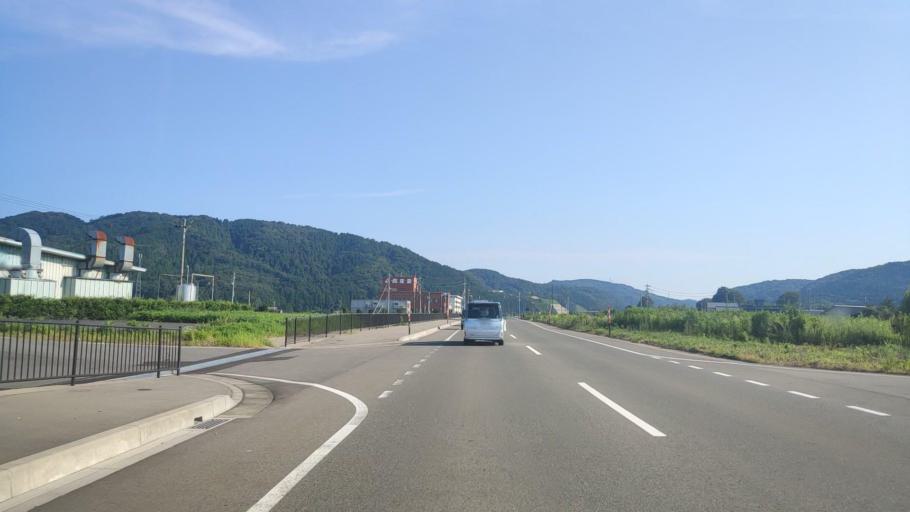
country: JP
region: Fukui
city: Maruoka
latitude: 36.1966
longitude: 136.2674
